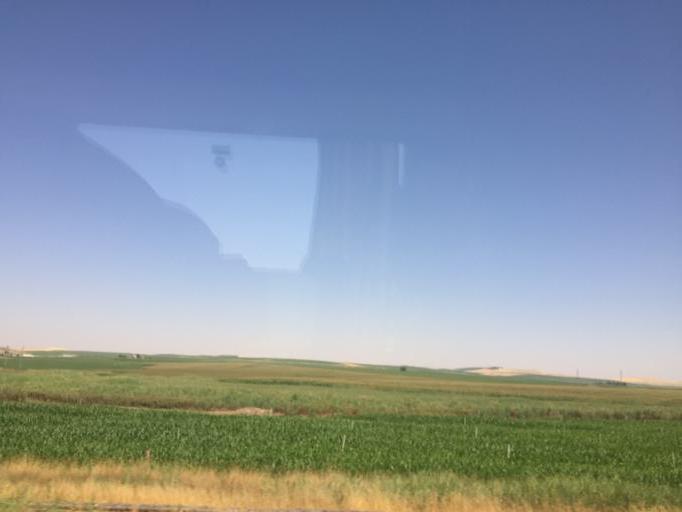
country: TR
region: Diyarbakir
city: Tepe
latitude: 37.8510
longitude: 40.7633
